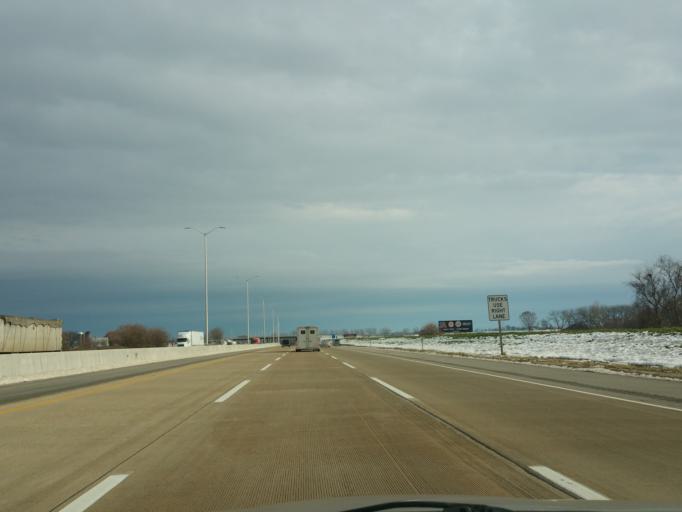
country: US
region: Illinois
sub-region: Boone County
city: Belvidere
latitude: 42.2224
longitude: -88.7574
